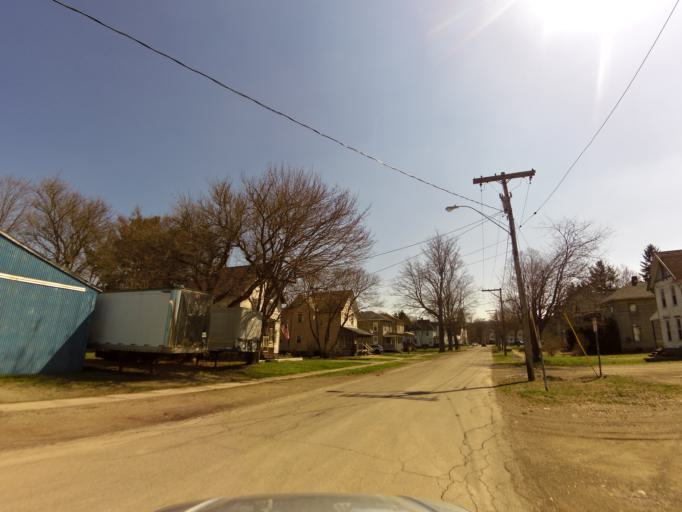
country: US
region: New York
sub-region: Cattaraugus County
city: Franklinville
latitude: 42.3355
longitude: -78.4617
